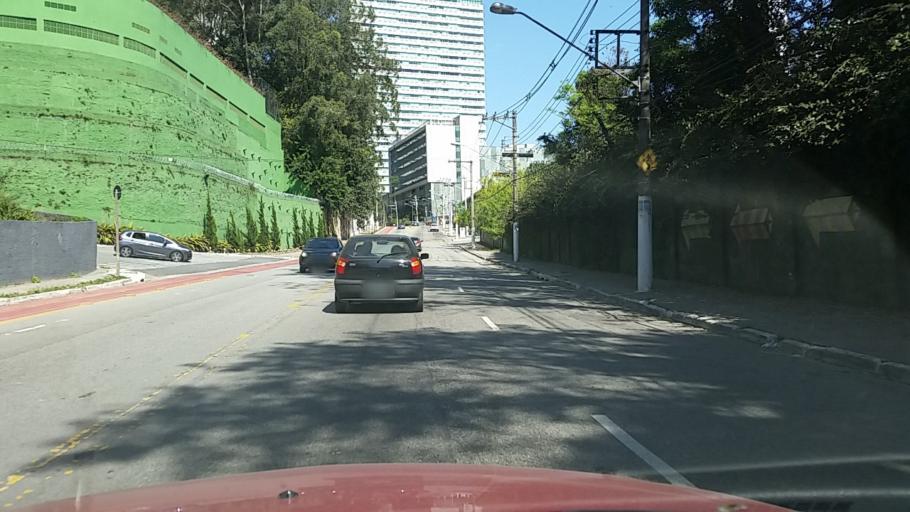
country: BR
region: Sao Paulo
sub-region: Taboao Da Serra
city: Taboao da Serra
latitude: -23.6191
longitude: -46.7429
